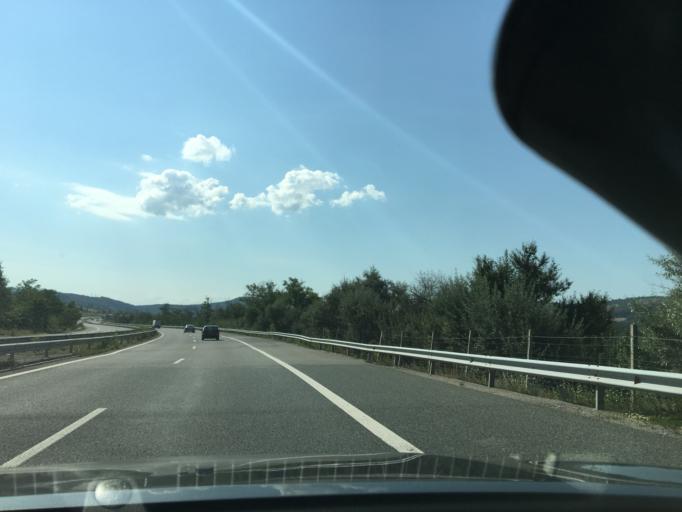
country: BG
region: Pernik
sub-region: Obshtina Pernik
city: Pernik
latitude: 42.5570
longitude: 23.1184
